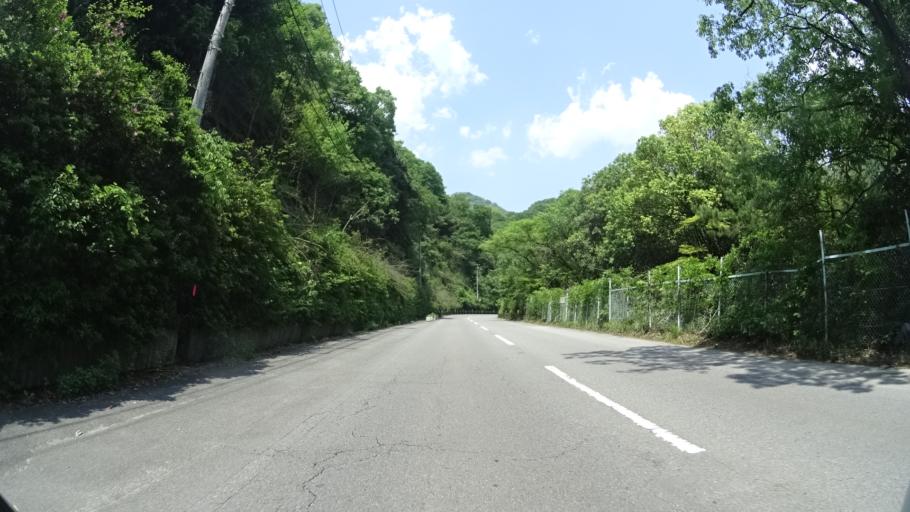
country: JP
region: Ehime
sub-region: Shikoku-chuo Shi
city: Matsuyama
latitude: 33.8683
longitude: 132.8274
